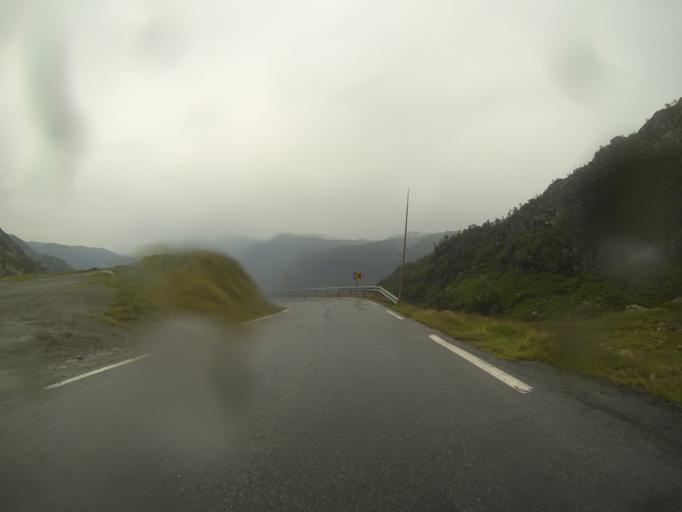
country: NO
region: Hordaland
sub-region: Odda
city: Odda
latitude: 59.7818
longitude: 6.7538
